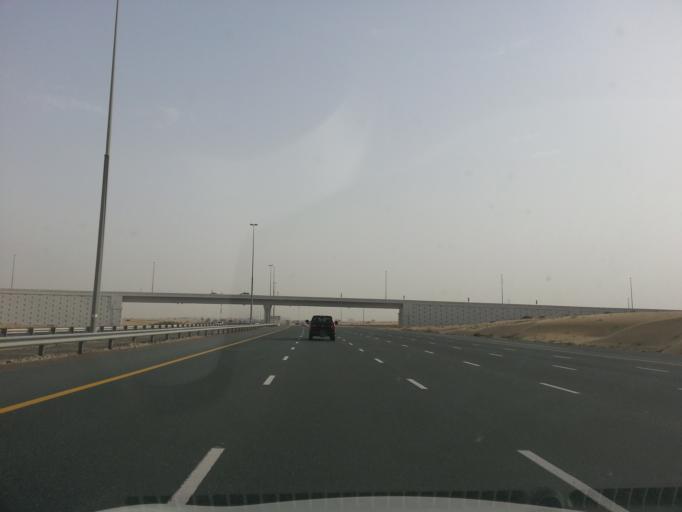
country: AE
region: Dubai
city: Dubai
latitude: 24.9793
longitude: 55.2409
